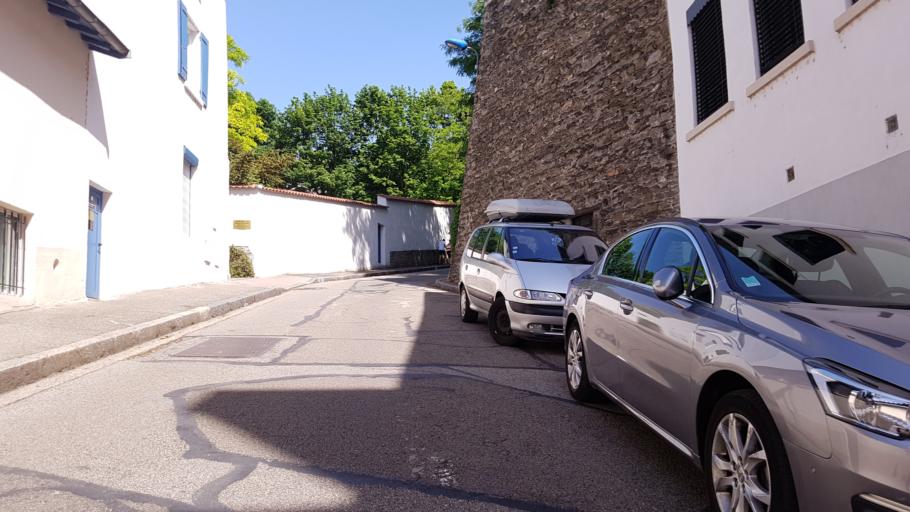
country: FR
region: Rhone-Alpes
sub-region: Departement du Rhone
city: Caluire-et-Cuire
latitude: 45.7887
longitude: 4.8532
